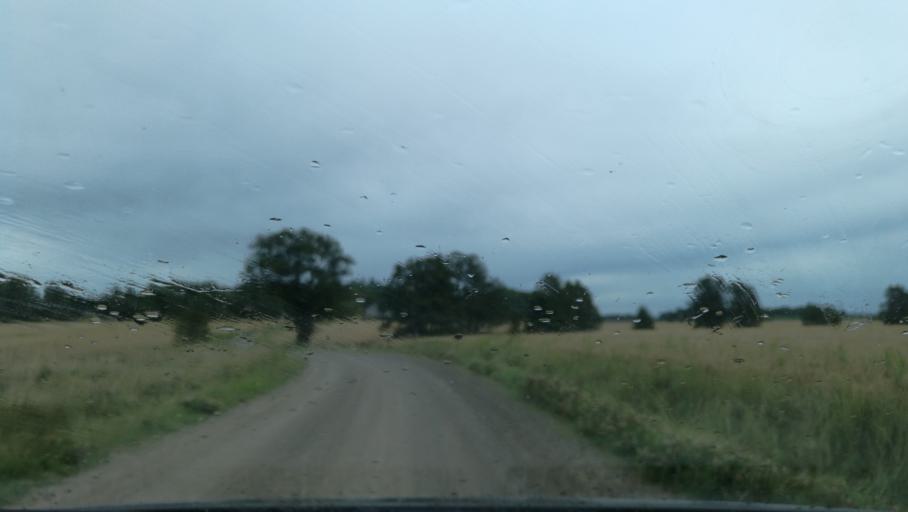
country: SE
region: Vaestmanland
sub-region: Vasteras
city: Tillberga
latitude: 59.7167
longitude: 16.6375
